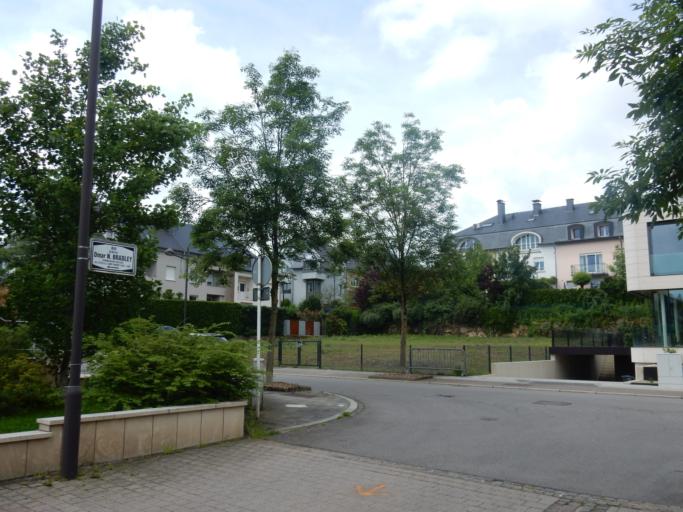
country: LU
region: Luxembourg
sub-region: Canton de Luxembourg
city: Strassen
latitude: 49.6071
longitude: 6.0990
